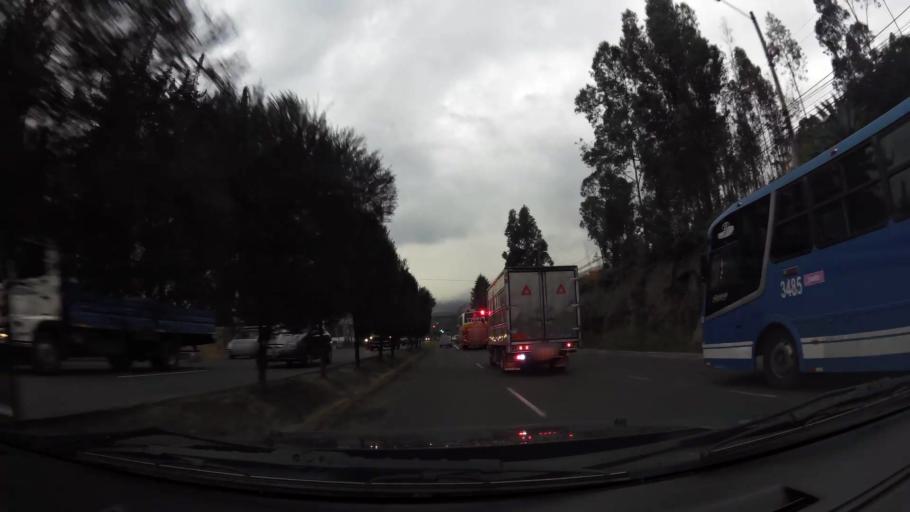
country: EC
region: Pichincha
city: Quito
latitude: -0.1034
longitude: -78.4630
